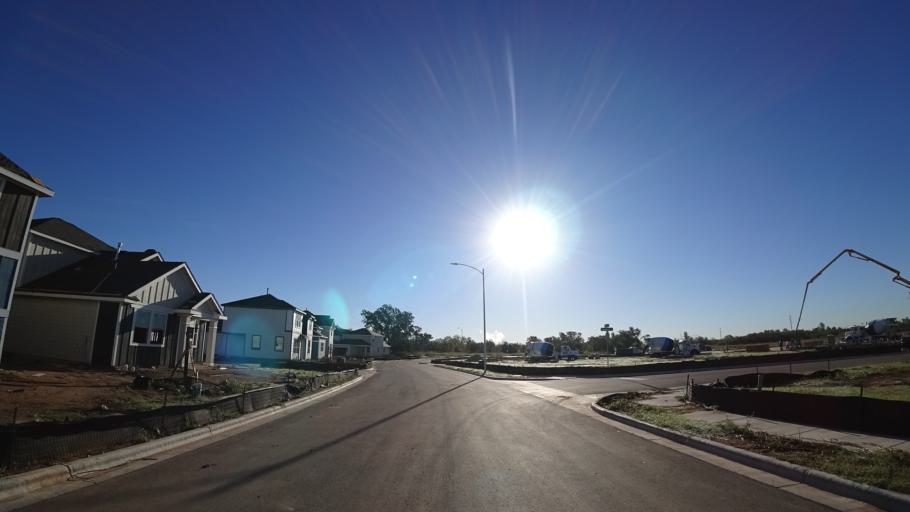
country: US
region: Texas
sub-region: Travis County
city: Hornsby Bend
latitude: 30.2186
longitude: -97.6347
